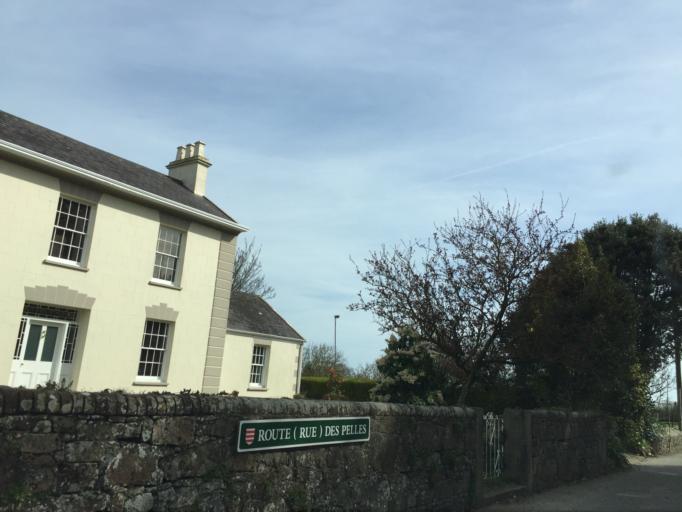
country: JE
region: St Helier
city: Saint Helier
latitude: 49.2292
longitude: -2.0440
